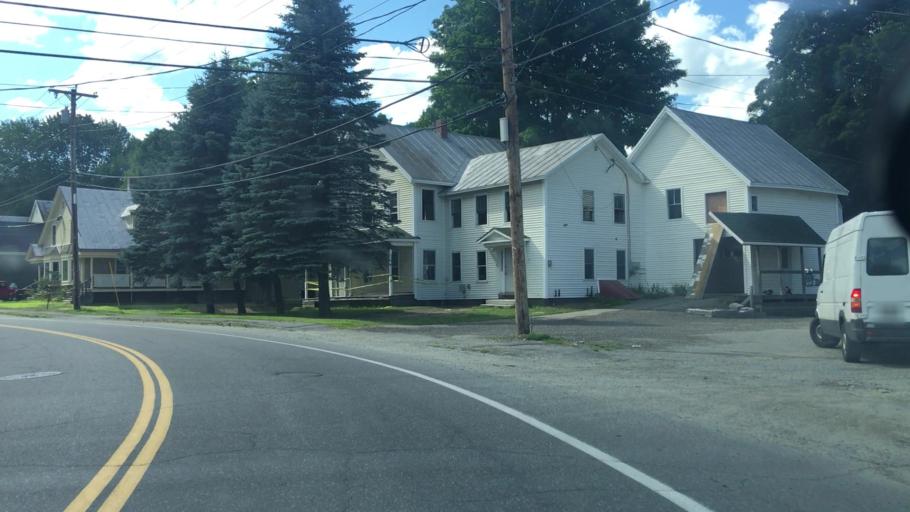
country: US
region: Maine
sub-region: Franklin County
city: Farmington
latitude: 44.6624
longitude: -70.1528
